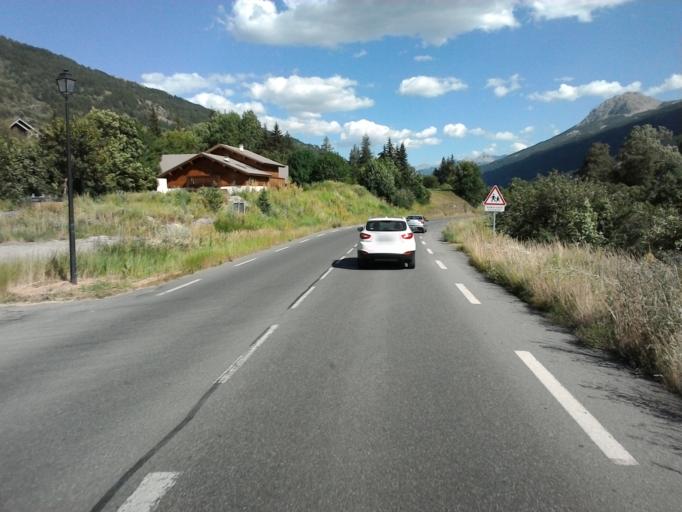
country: FR
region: Provence-Alpes-Cote d'Azur
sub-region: Departement des Hautes-Alpes
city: Le Monetier-les-Bains
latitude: 44.9649
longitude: 6.5352
